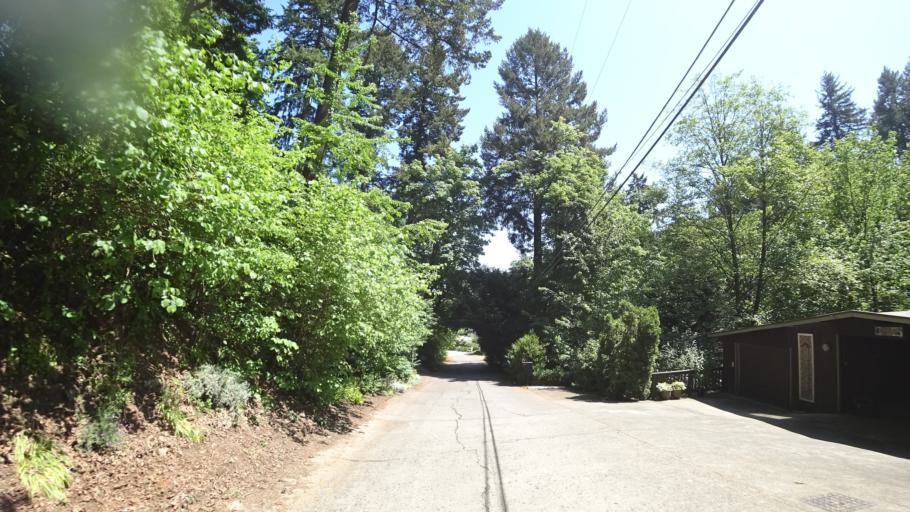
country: US
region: Oregon
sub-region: Multnomah County
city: Portland
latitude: 45.4762
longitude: -122.6823
